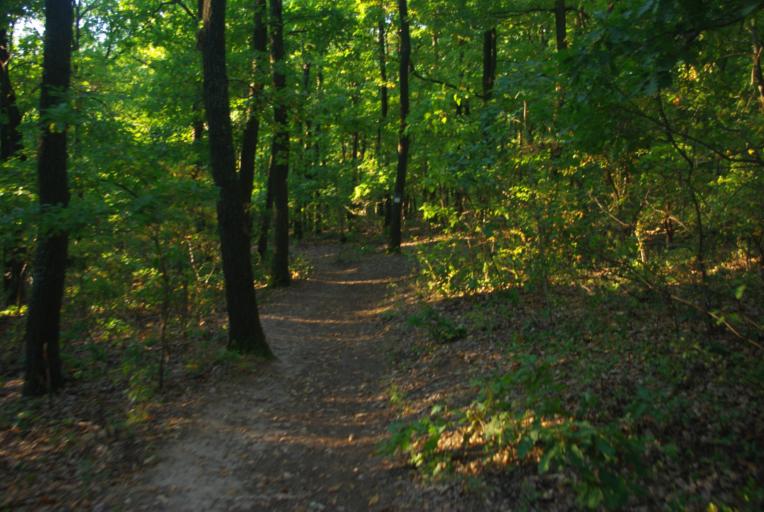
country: HU
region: Heves
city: Gyongyossolymos
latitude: 47.8334
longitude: 19.9606
